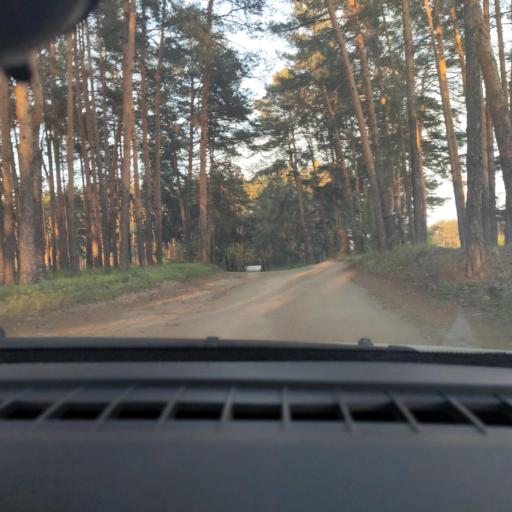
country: RU
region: Voronezj
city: Shilovo
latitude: 51.5347
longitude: 39.1362
